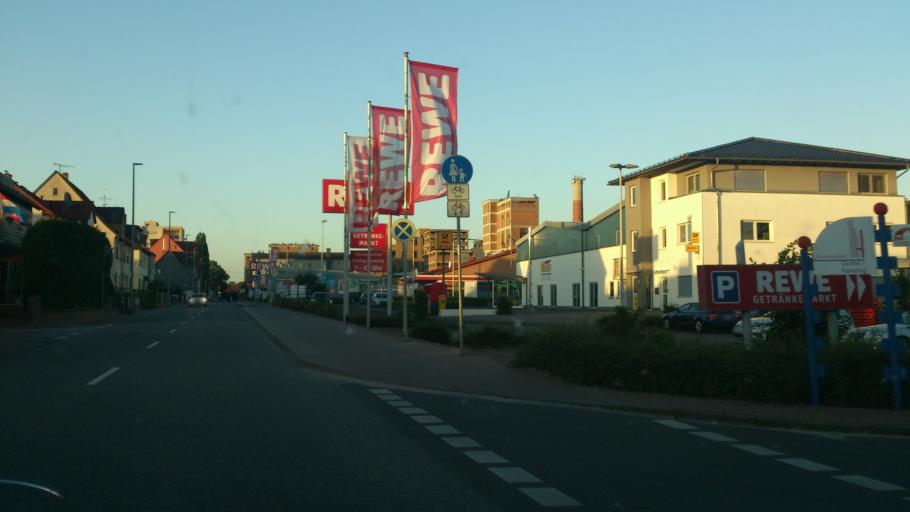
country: DE
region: Hesse
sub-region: Regierungsbezirk Darmstadt
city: Hattersheim
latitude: 50.0496
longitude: 8.4920
